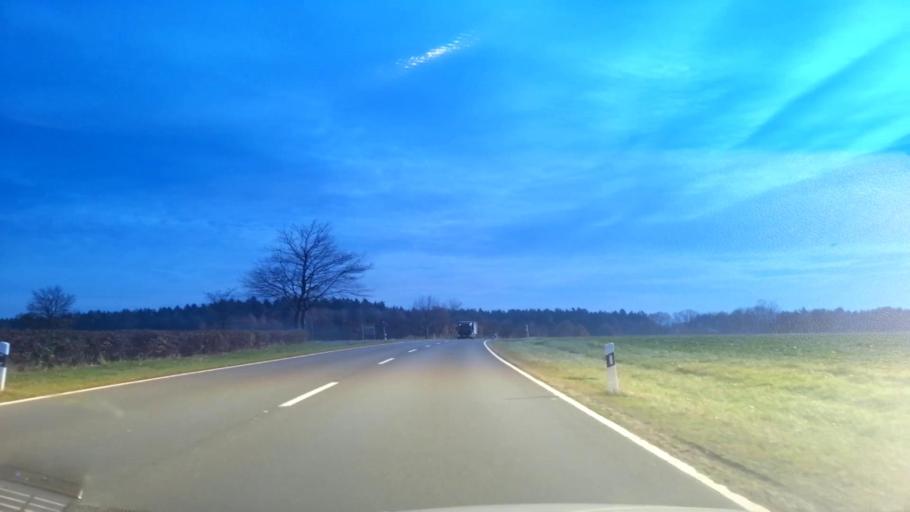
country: DE
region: Bavaria
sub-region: Upper Palatinate
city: Plossberg
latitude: 49.9132
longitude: 11.8442
